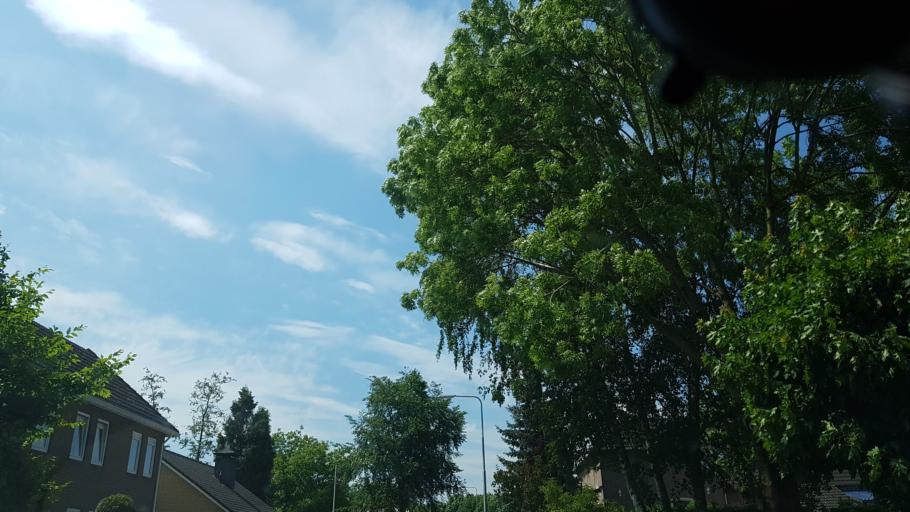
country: NL
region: Gelderland
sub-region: Gemeente Wijchen
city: Bergharen
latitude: 51.8895
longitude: 5.6641
